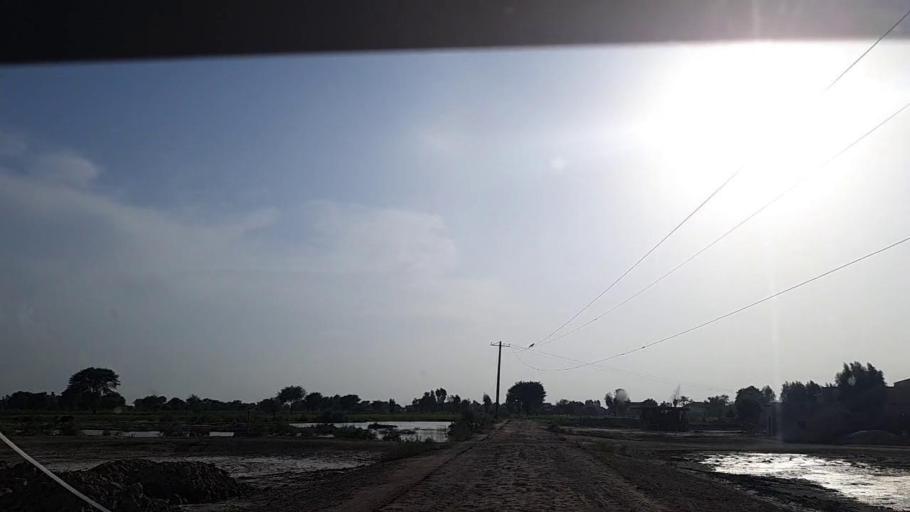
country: PK
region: Sindh
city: Khanpur
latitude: 27.8300
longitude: 69.3771
